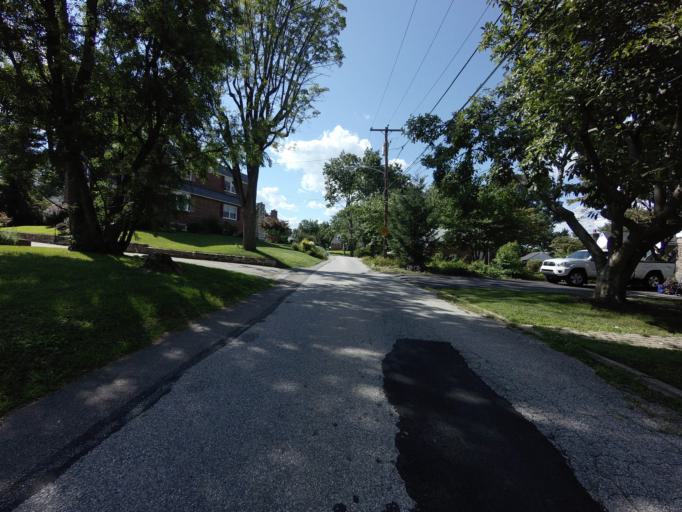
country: US
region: Pennsylvania
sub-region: Montgomery County
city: Bala-Cynwyd
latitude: 40.0249
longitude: -75.2036
